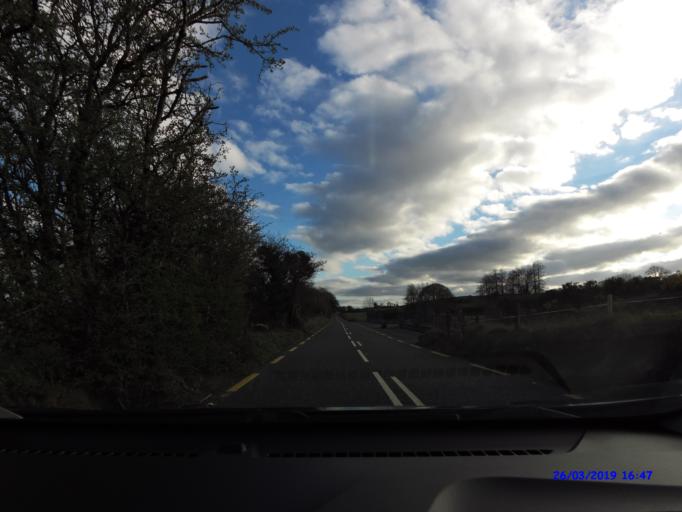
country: IE
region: Connaught
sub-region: Maigh Eo
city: Ballyhaunis
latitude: 53.8215
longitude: -8.7636
